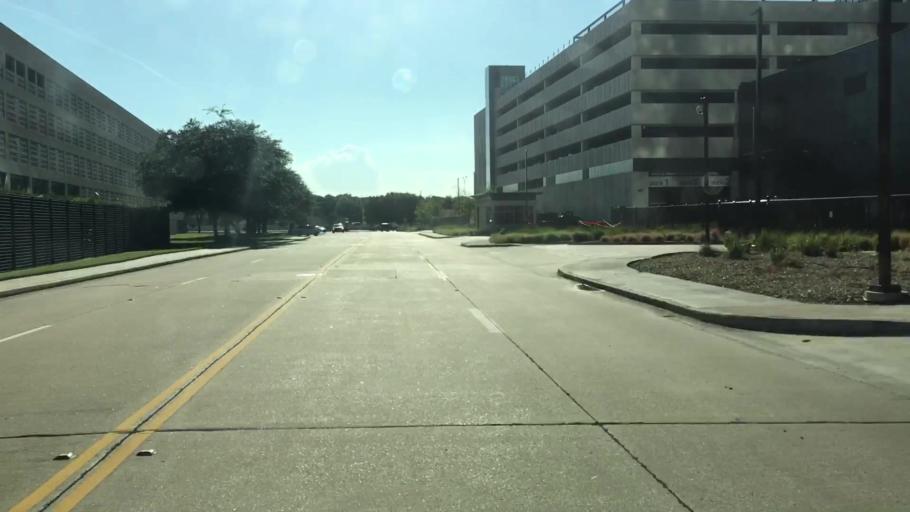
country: US
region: Texas
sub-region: Harris County
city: Bunker Hill Village
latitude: 29.7415
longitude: -95.5607
